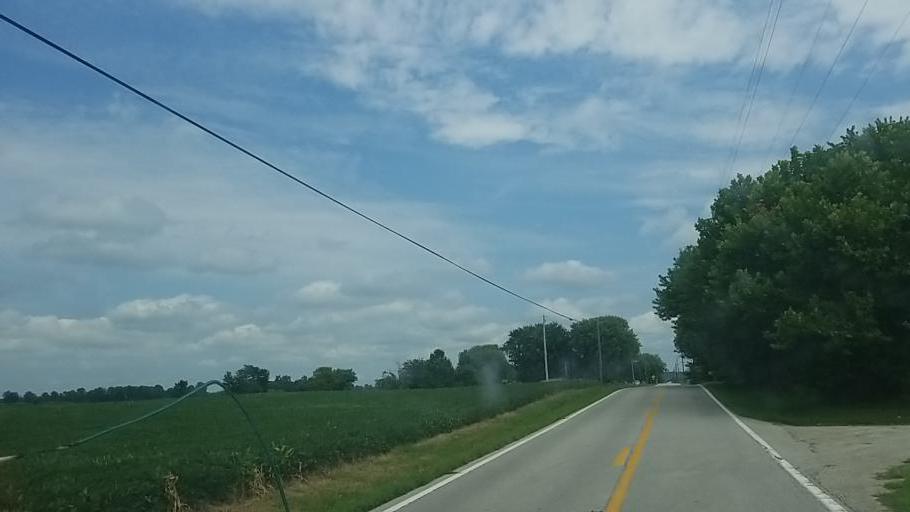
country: US
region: Ohio
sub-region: Franklin County
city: Groveport
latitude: 39.7985
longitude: -82.8916
